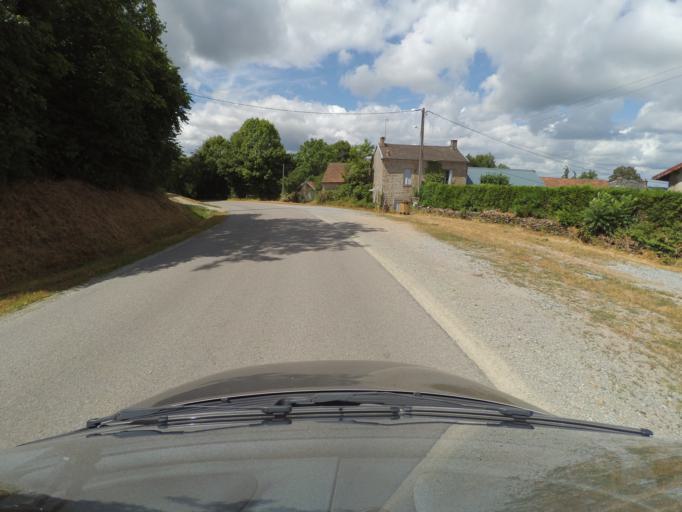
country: FR
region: Limousin
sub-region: Departement de la Creuse
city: Bourganeuf
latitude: 45.9319
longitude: 1.8114
